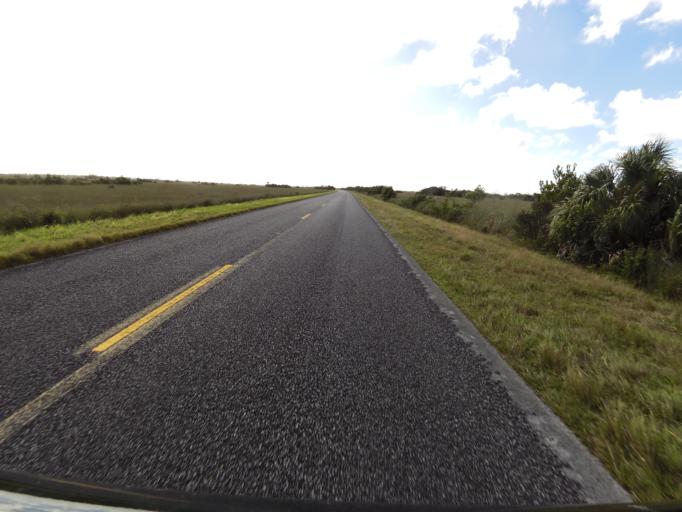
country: US
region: Florida
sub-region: Miami-Dade County
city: Florida City
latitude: 25.3909
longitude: -80.8027
